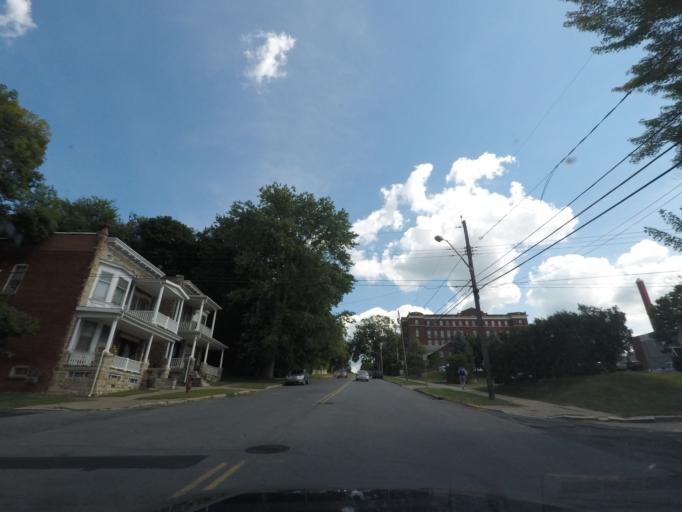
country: US
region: New York
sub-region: Rensselaer County
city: Troy
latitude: 42.7338
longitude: -73.6814
